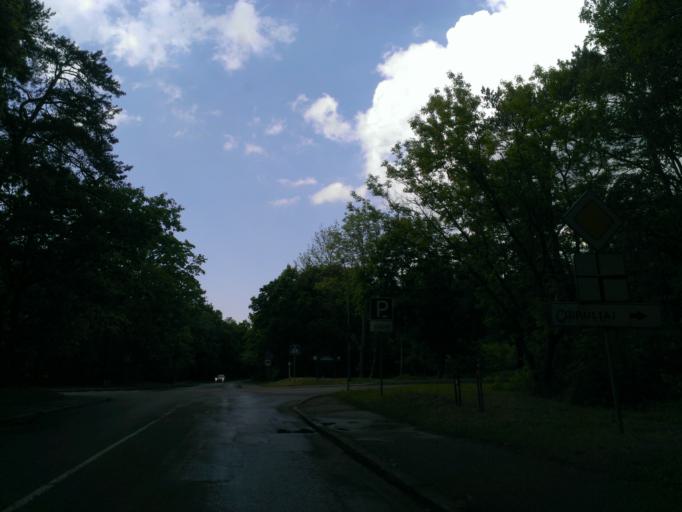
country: LT
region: Klaipedos apskritis
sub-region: Klaipeda
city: Klaipeda
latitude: 55.7657
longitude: 21.0871
